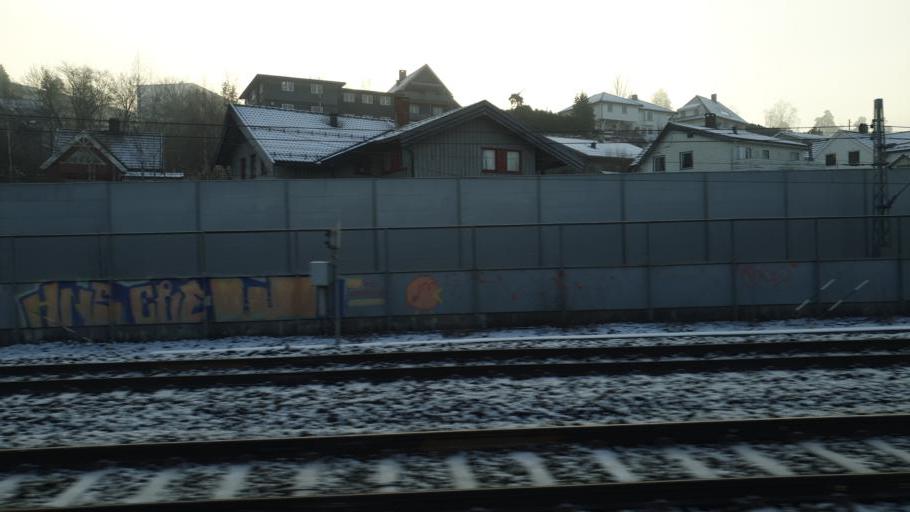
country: NO
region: Akershus
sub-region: Baerum
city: Sandvika
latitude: 59.8910
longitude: 10.5102
